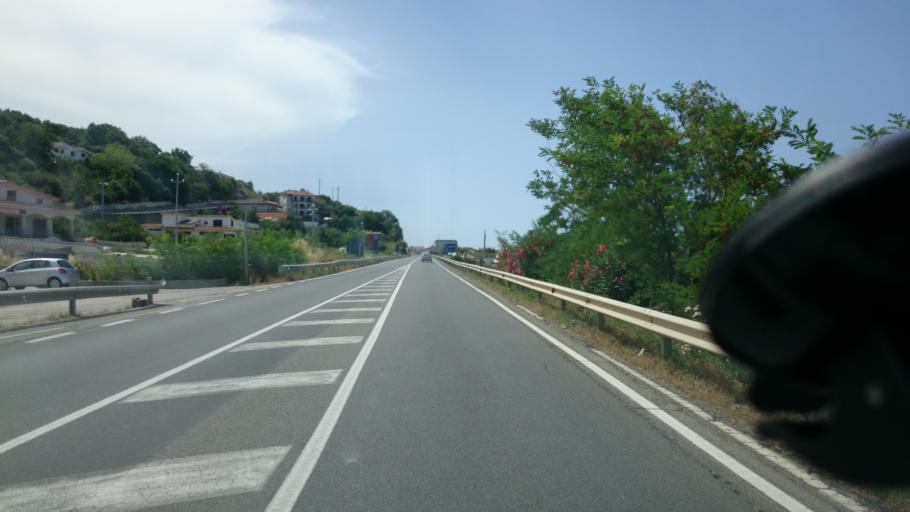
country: IT
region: Calabria
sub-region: Provincia di Cosenza
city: Diamante
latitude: 39.6842
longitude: 15.8198
